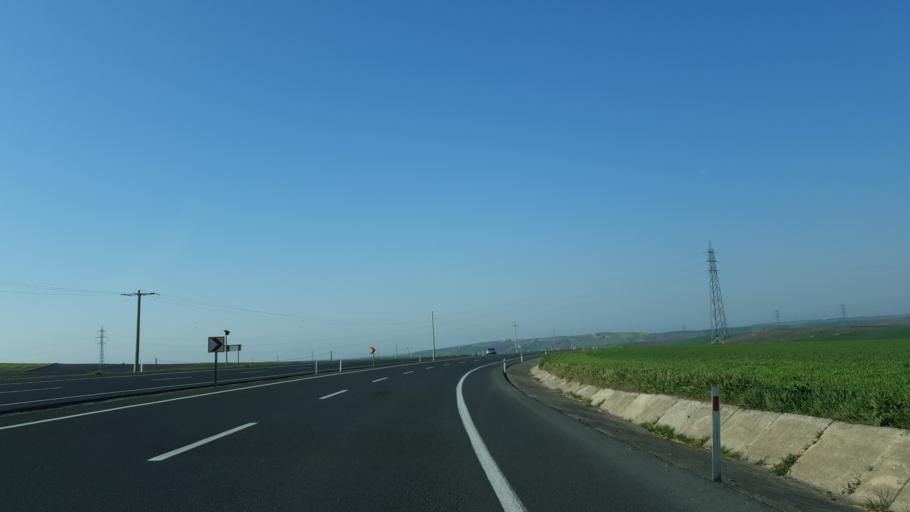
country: TR
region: Tekirdag
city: Corlu
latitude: 41.0998
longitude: 27.7544
